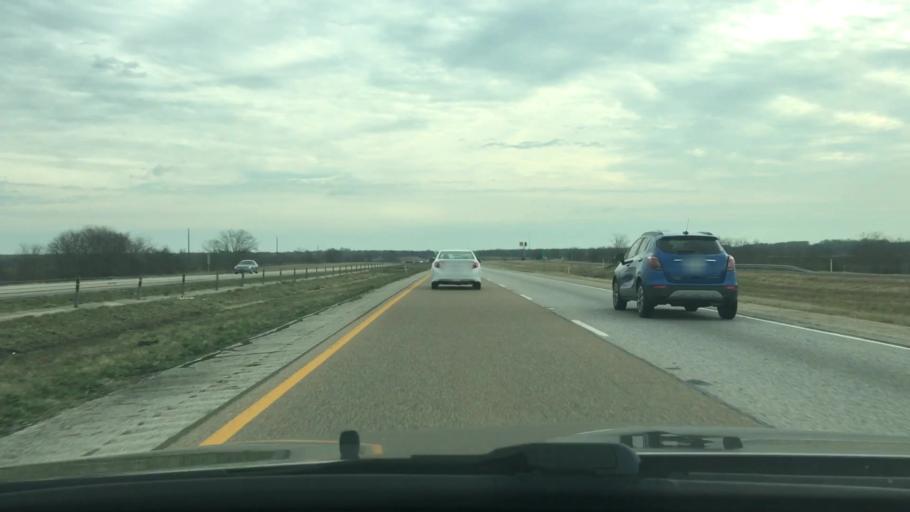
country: US
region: Texas
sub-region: Leon County
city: Centerville
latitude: 31.1032
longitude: -95.9648
